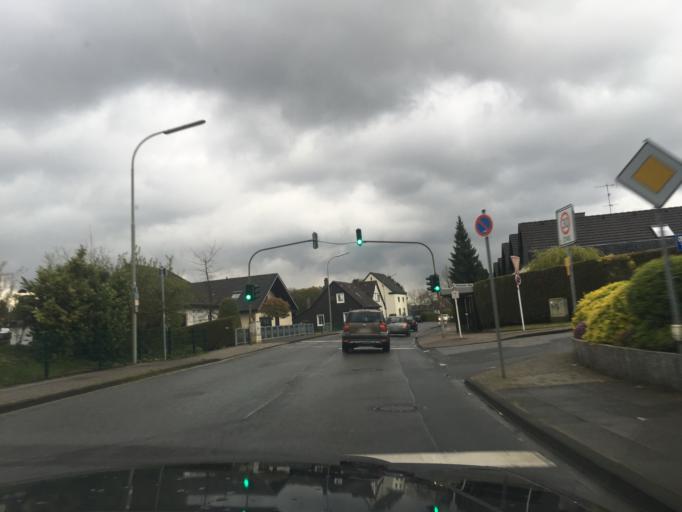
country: DE
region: North Rhine-Westphalia
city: Burscheid
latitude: 51.1182
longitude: 7.1207
